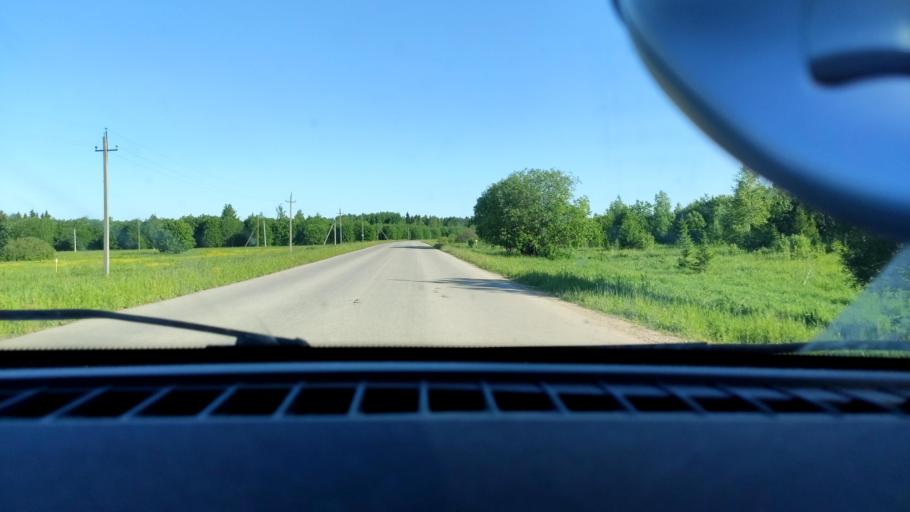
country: RU
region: Perm
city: Polazna
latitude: 58.1977
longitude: 56.5338
